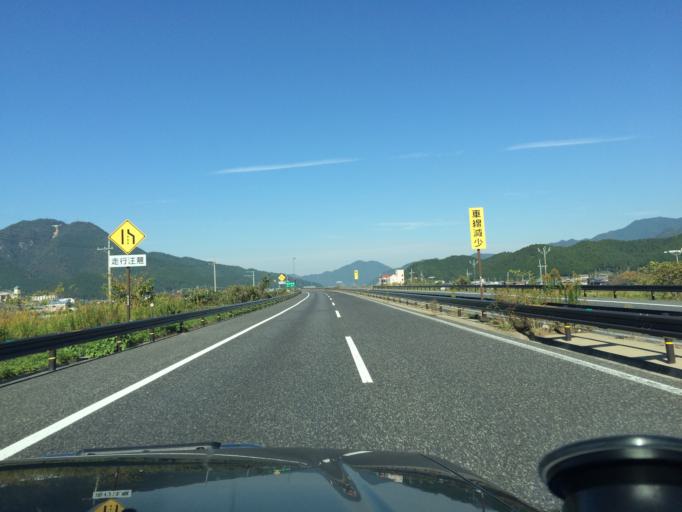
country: JP
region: Kyoto
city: Fukuchiyama
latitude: 35.1685
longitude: 135.0434
